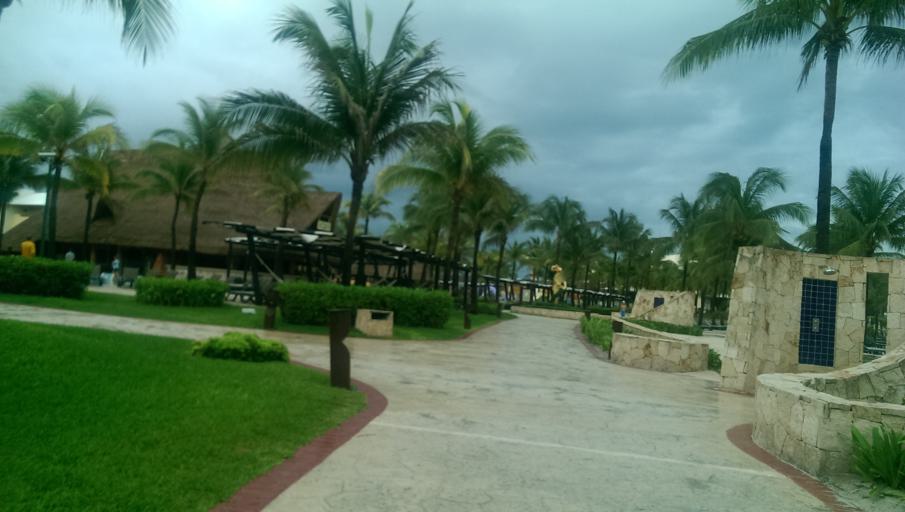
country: MX
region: Quintana Roo
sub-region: Tulum
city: Ciudad Chemuyil
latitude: 20.4896
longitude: -87.2391
